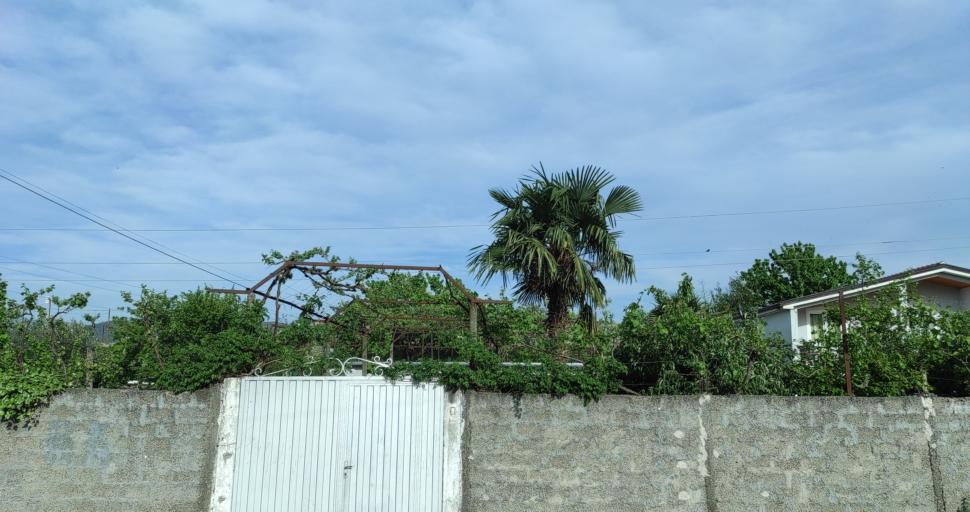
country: AL
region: Shkoder
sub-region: Rrethi i Shkodres
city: Shkoder
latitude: 42.0709
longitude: 19.5293
